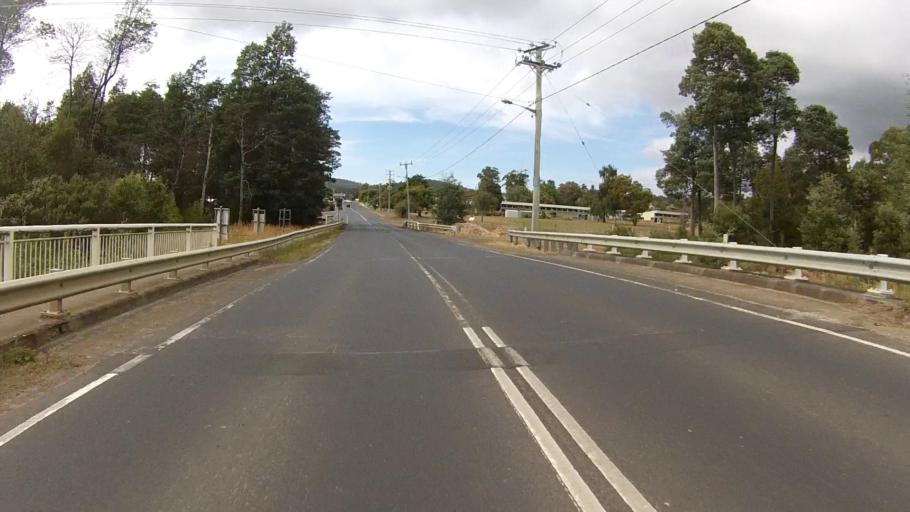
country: AU
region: Tasmania
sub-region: Kingborough
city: Margate
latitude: -43.0635
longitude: 147.2537
